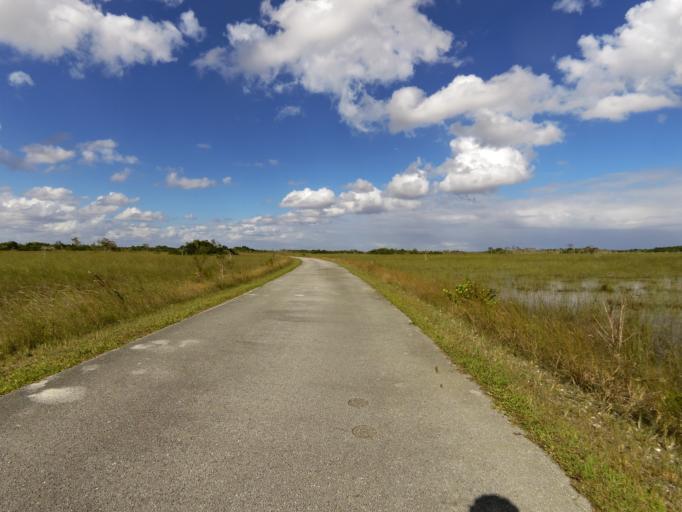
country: US
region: Florida
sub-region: Miami-Dade County
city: The Hammocks
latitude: 25.7147
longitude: -80.7592
